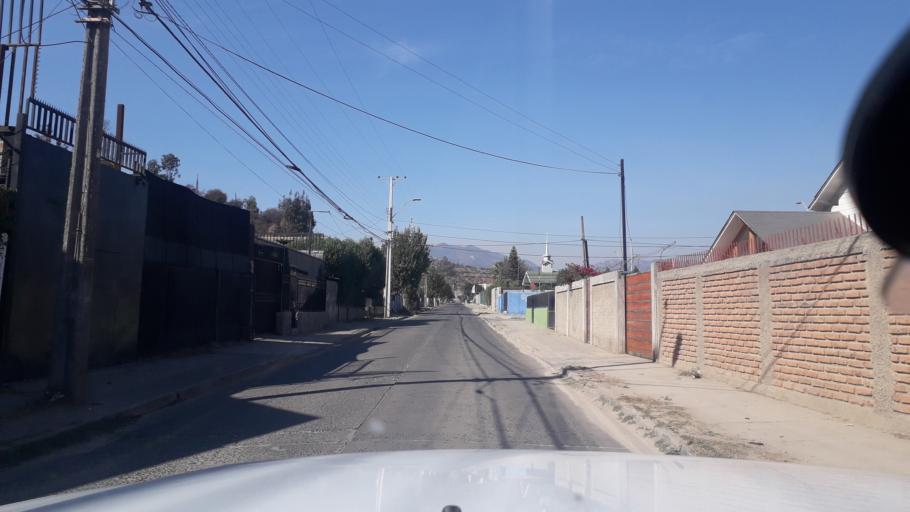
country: CL
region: Valparaiso
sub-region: Provincia de Marga Marga
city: Villa Alemana
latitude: -33.0444
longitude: -71.3497
